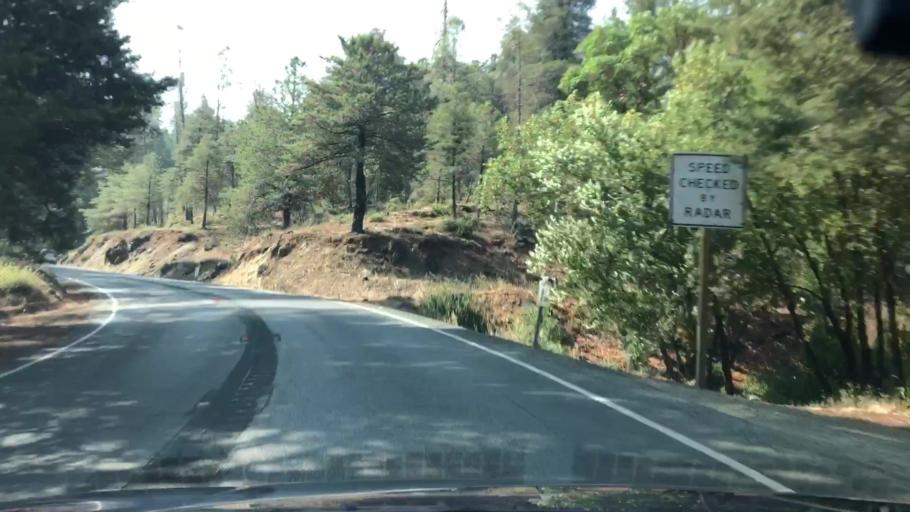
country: US
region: California
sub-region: Lake County
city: Middletown
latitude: 38.6754
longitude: -122.5922
